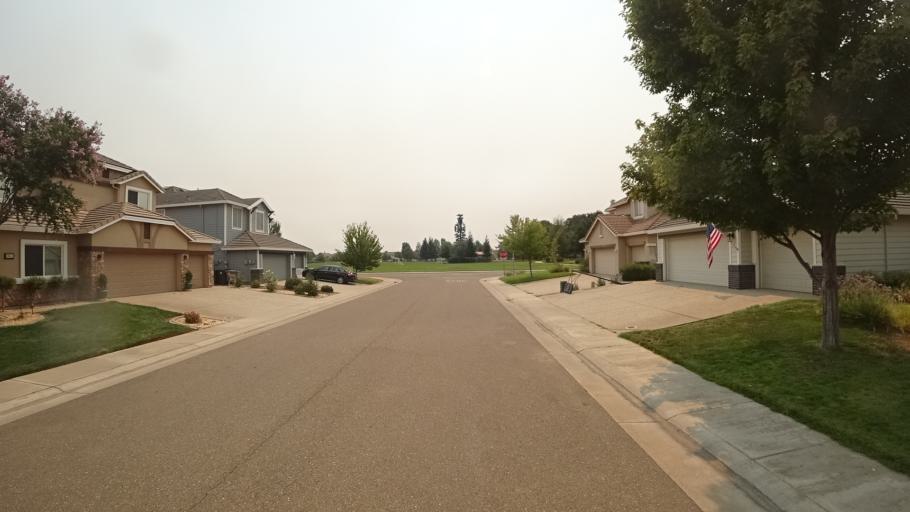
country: US
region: California
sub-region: Sacramento County
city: Laguna
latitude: 38.4069
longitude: -121.4238
